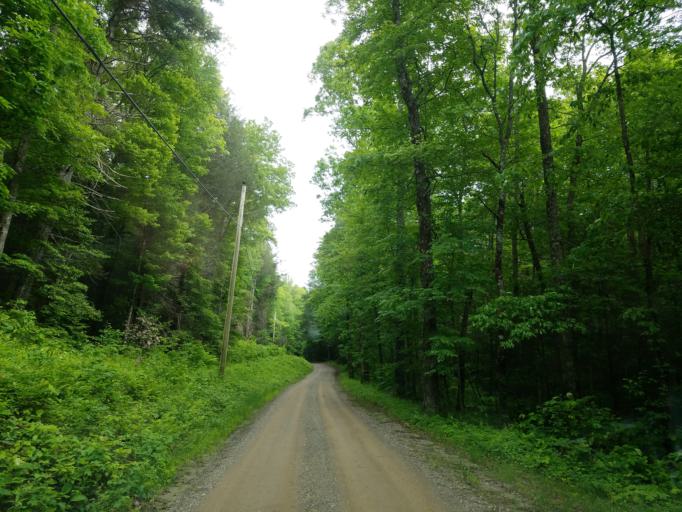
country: US
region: Georgia
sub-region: Union County
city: Blairsville
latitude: 34.7340
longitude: -83.9714
